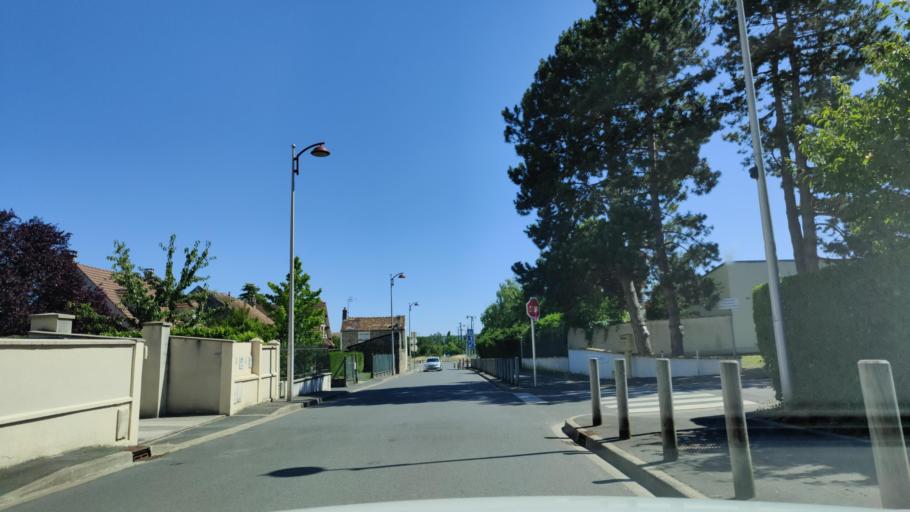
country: FR
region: Ile-de-France
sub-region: Departement de l'Essonne
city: Bruyeres-le-Chatel
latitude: 48.5890
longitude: 2.1894
